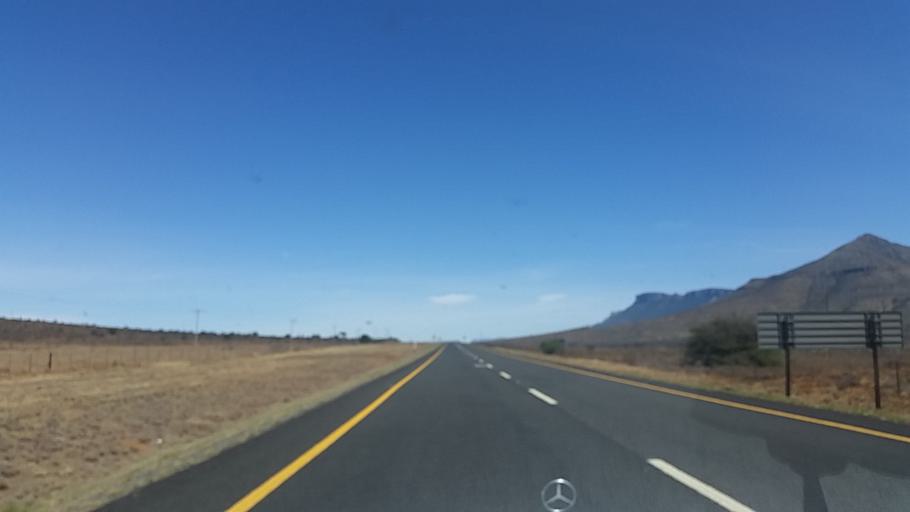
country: ZA
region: Eastern Cape
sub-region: Cacadu District Municipality
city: Graaff-Reinet
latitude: -32.3533
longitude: 24.3058
